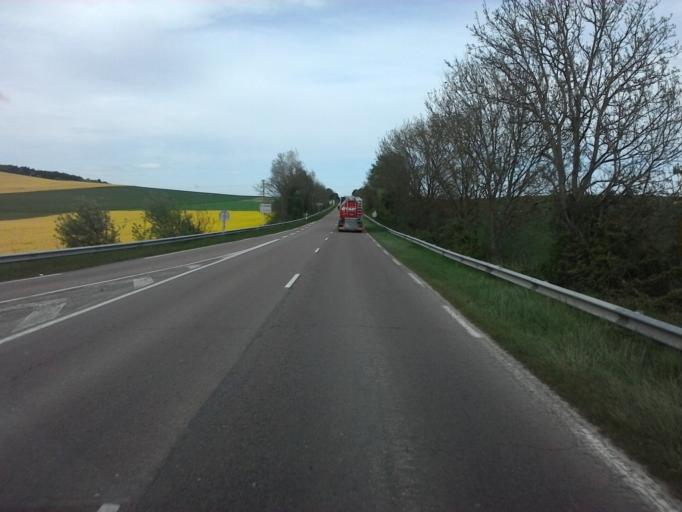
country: FR
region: Champagne-Ardenne
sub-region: Departement de l'Aube
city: Ervy-le-Chatel
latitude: 48.1144
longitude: 3.9381
